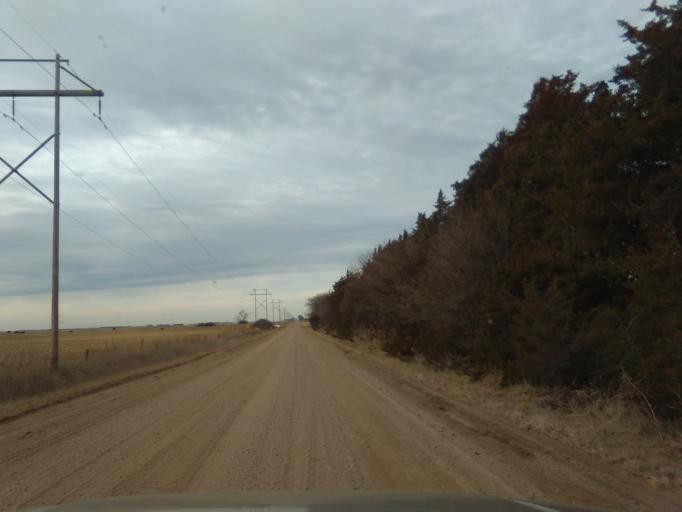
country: US
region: Nebraska
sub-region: Buffalo County
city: Shelton
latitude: 40.6548
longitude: -98.7272
